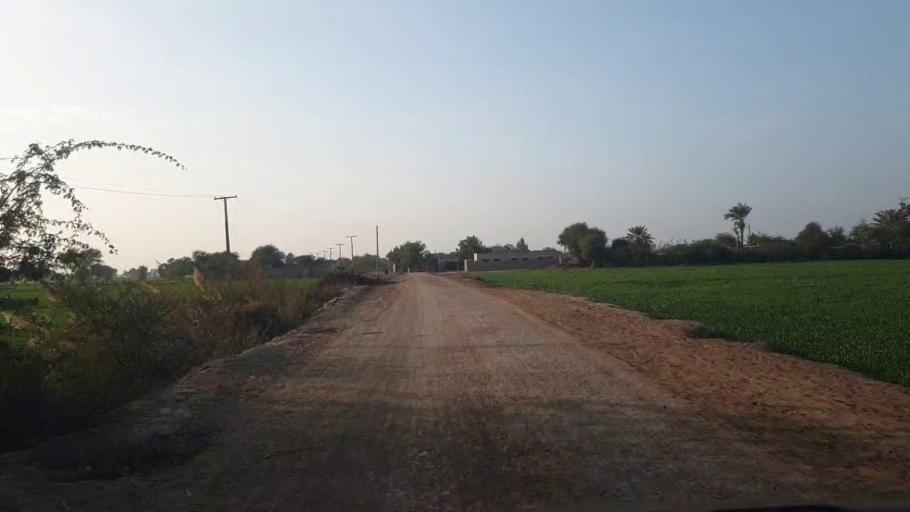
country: PK
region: Sindh
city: Berani
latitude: 25.8604
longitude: 68.7359
